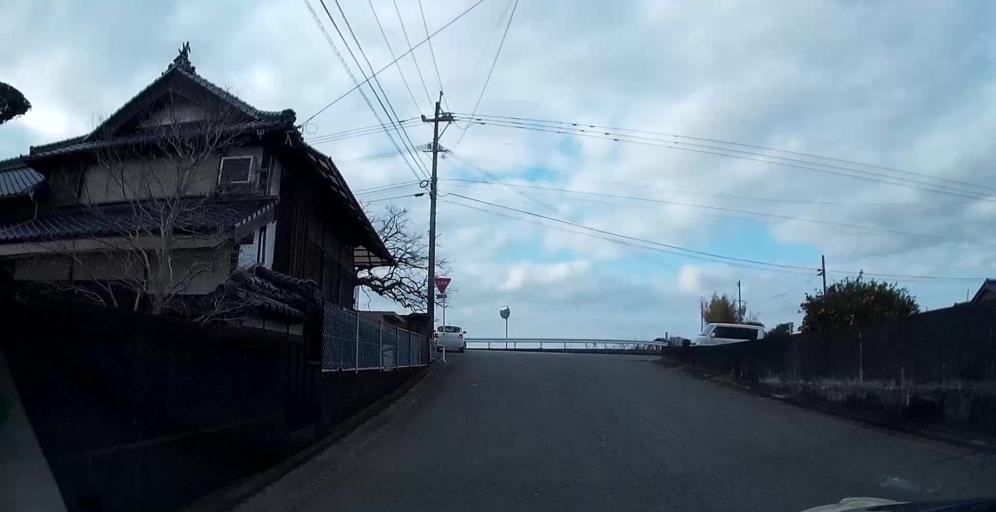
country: JP
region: Kumamoto
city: Yatsushiro
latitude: 32.5531
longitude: 130.6235
